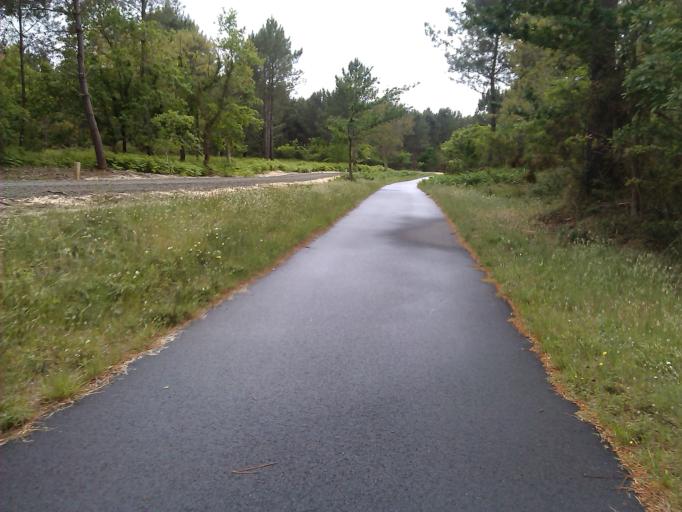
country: FR
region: Aquitaine
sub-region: Departement des Landes
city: Vielle-Saint-Girons
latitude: 43.9272
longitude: -1.3518
